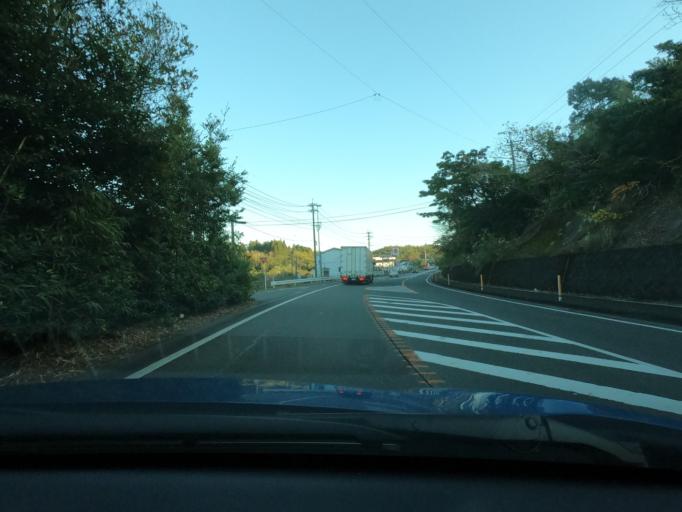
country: JP
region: Kagoshima
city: Satsumasendai
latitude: 31.8435
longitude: 130.2795
